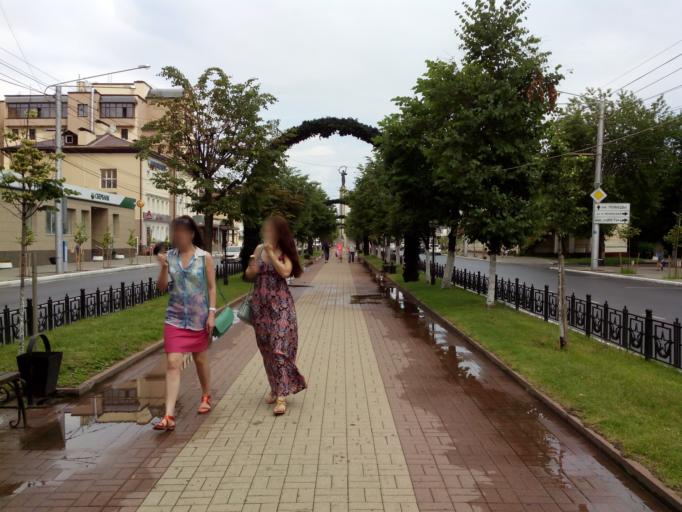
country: RU
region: Kaluga
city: Kaluga
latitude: 54.5131
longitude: 36.2684
